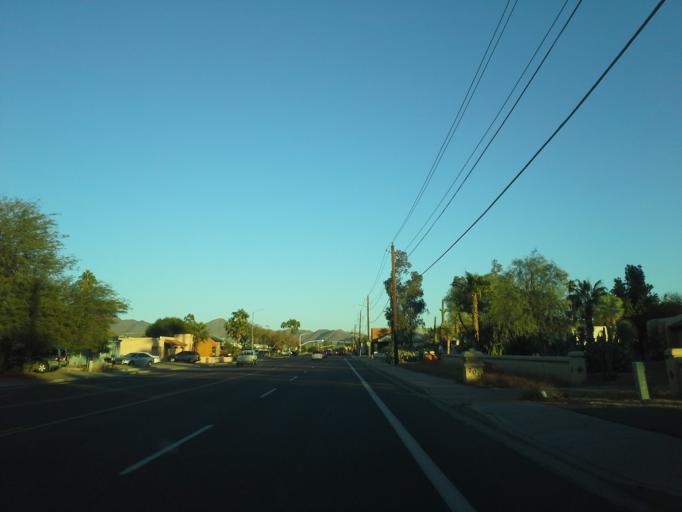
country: US
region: Arizona
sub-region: Maricopa County
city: Paradise Valley
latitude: 33.6112
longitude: -111.9297
